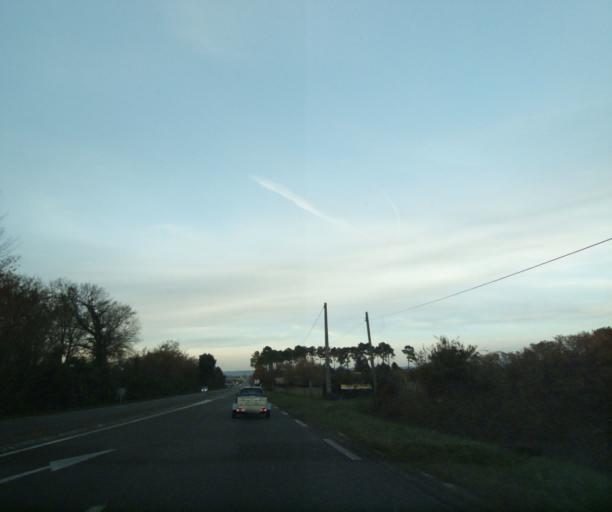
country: FR
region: Aquitaine
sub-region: Departement de la Gironde
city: Langon
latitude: 44.5123
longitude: -0.2390
